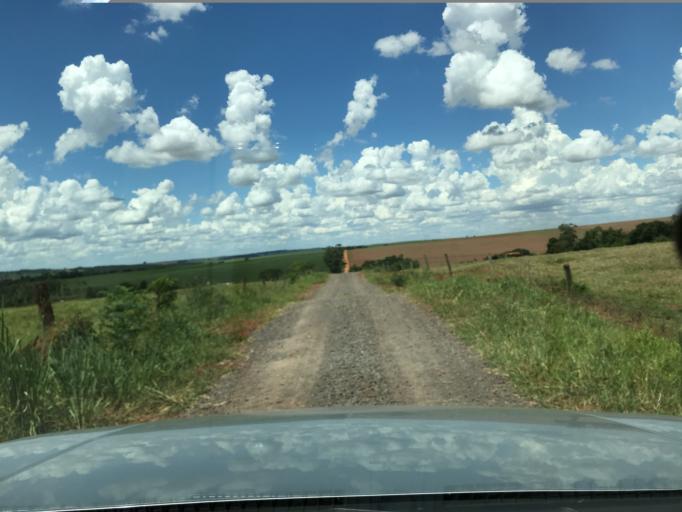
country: BR
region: Parana
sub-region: Palotina
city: Palotina
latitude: -24.1777
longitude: -53.7748
